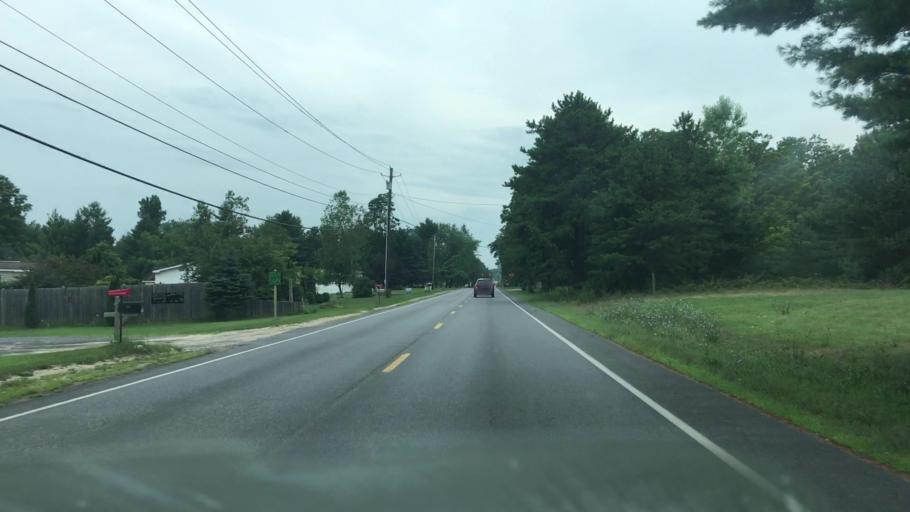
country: US
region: New York
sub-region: Clinton County
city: Plattsburgh West
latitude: 44.6562
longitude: -73.5107
